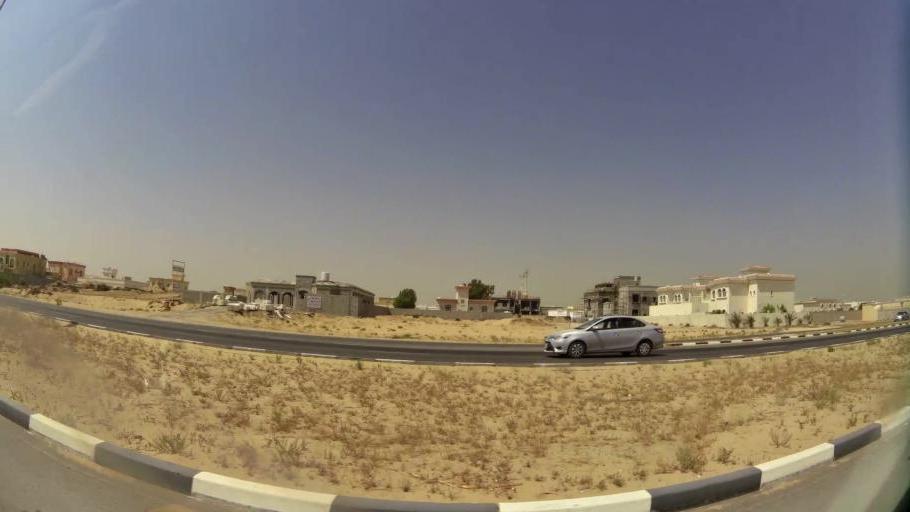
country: AE
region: Ajman
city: Ajman
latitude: 25.4244
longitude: 55.5271
